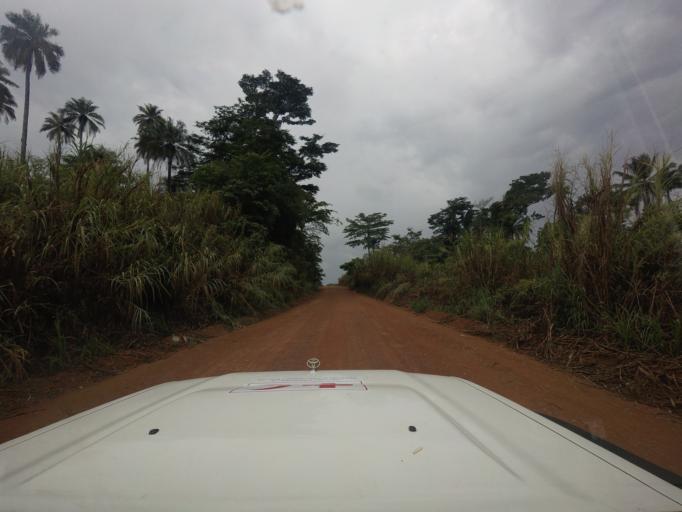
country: SL
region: Eastern Province
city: Buedu
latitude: 8.2924
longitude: -10.1339
